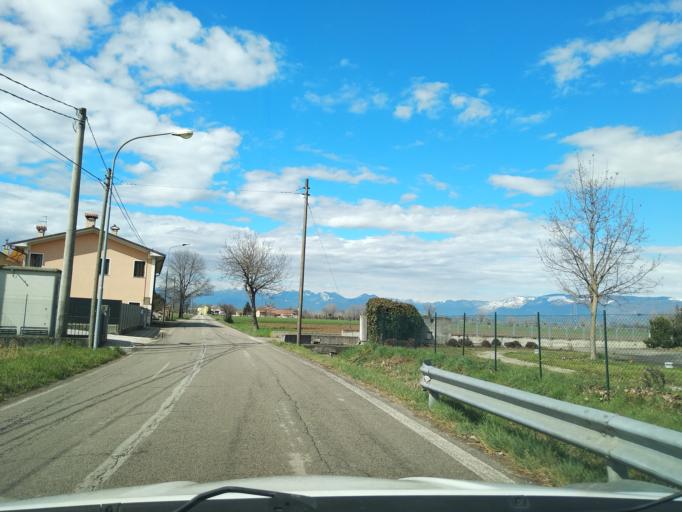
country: IT
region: Veneto
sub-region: Provincia di Vicenza
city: Bolzano Vicentino
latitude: 45.6077
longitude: 11.6097
